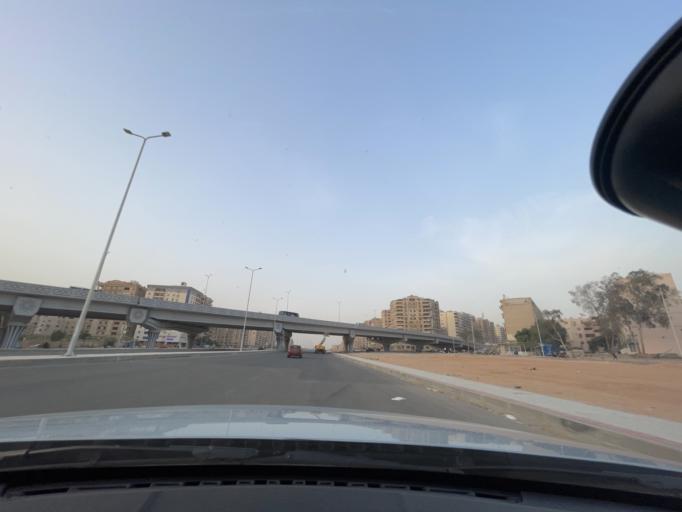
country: EG
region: Muhafazat al Qahirah
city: Cairo
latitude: 30.0470
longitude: 31.3654
